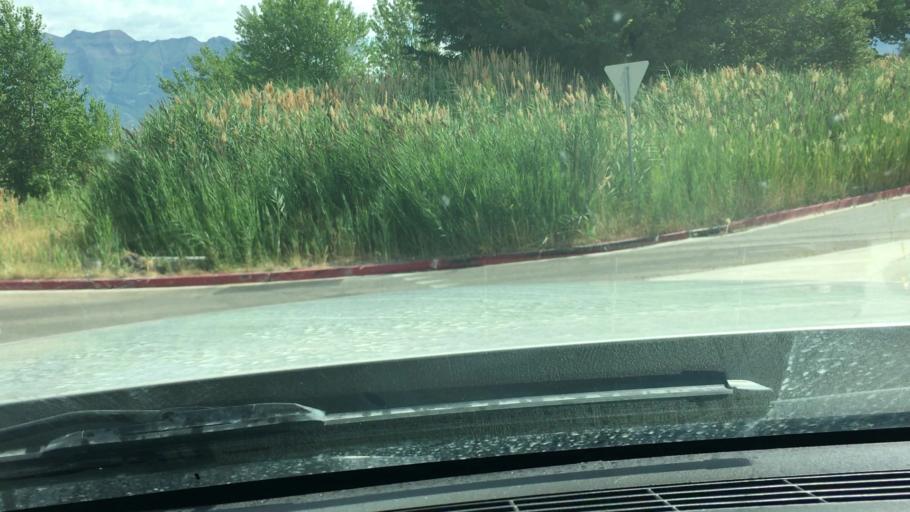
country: US
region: Utah
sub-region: Utah County
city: Orem
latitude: 40.2830
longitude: -111.7427
